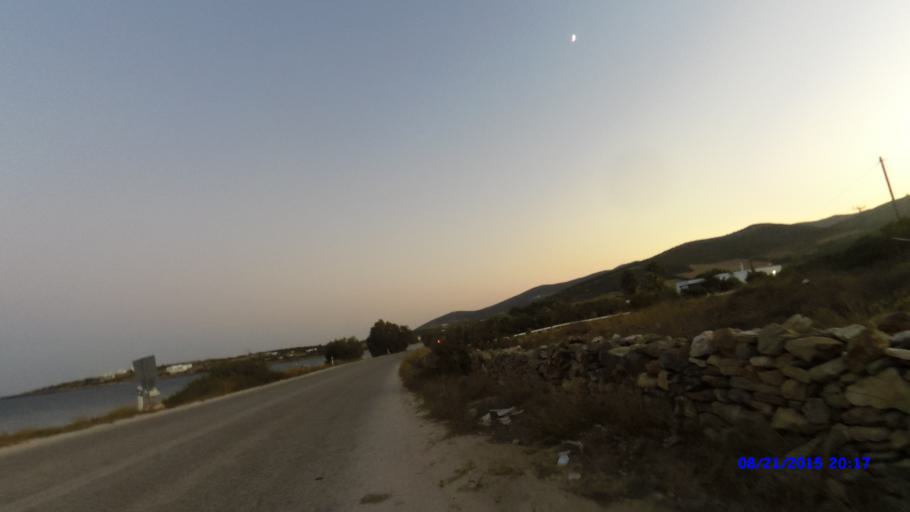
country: GR
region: South Aegean
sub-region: Nomos Kykladon
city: Antiparos
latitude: 37.0093
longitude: 25.0747
